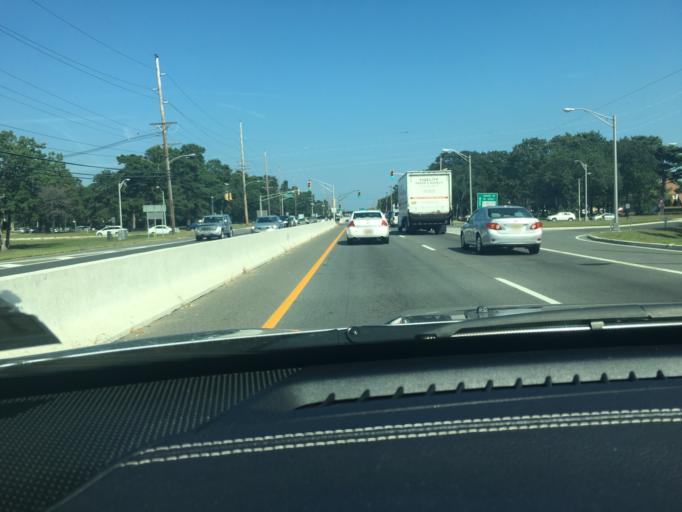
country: US
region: New Jersey
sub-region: Ocean County
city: Leisure Village
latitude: 40.0528
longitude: -74.1801
